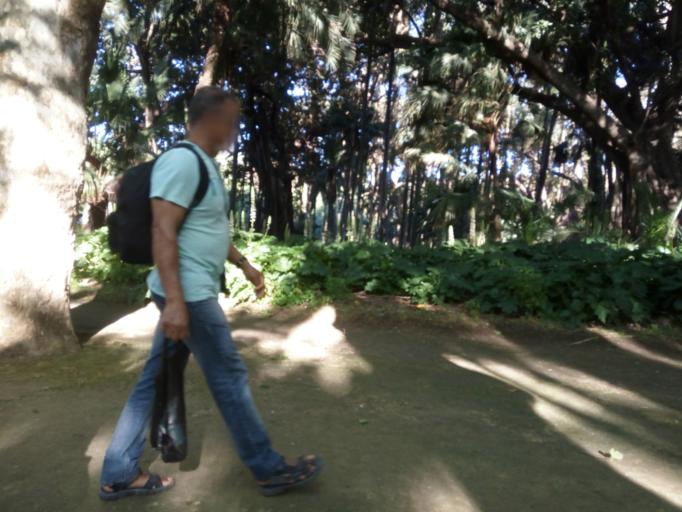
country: DZ
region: Alger
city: Algiers
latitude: 36.7481
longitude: 3.0744
